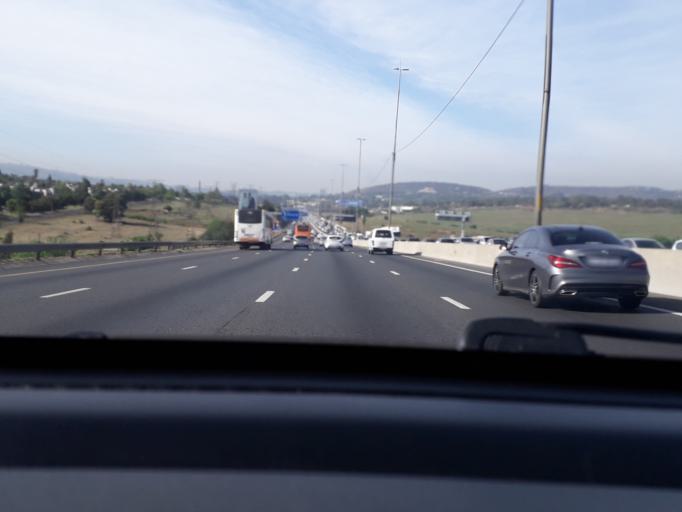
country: ZA
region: Gauteng
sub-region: City of Johannesburg Metropolitan Municipality
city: Modderfontein
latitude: -26.1342
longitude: 28.1333
